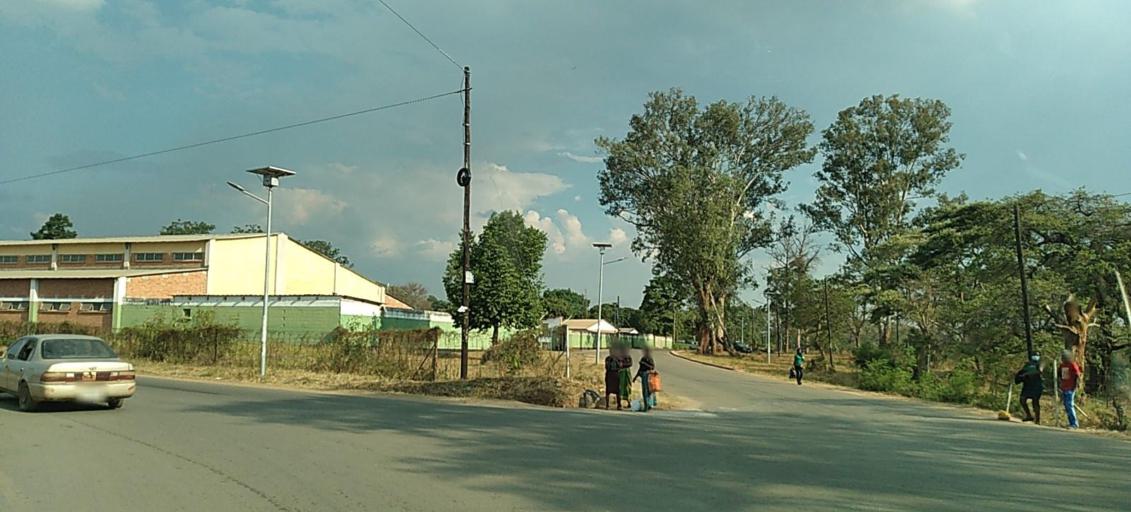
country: ZM
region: Lusaka
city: Lusaka
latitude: -15.5458
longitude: 28.2472
